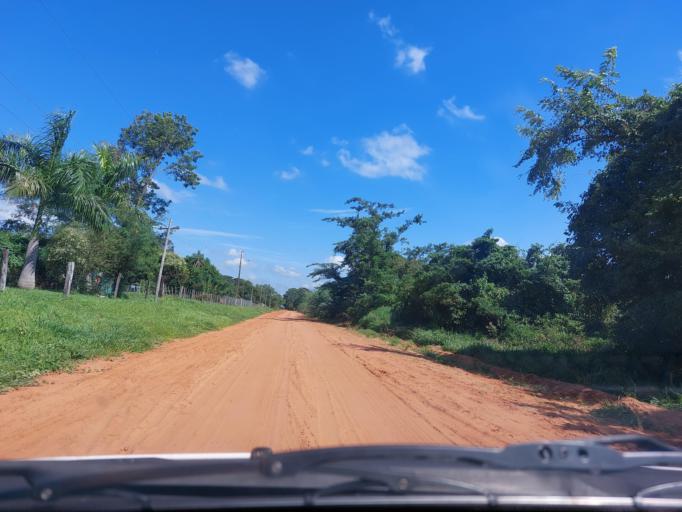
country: PY
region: San Pedro
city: Itacurubi del Rosario
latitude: -24.5348
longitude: -56.5771
